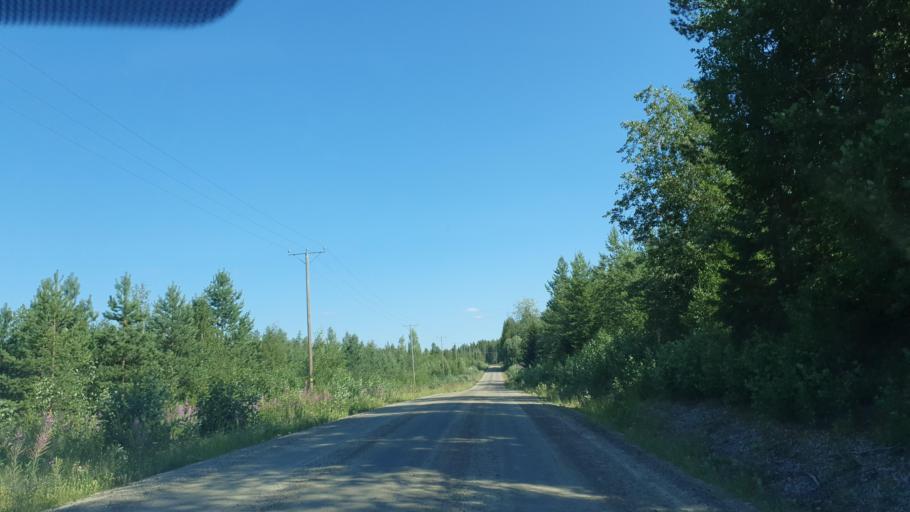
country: FI
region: Kainuu
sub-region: Kehys-Kainuu
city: Kuhmo
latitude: 64.0495
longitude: 29.6151
